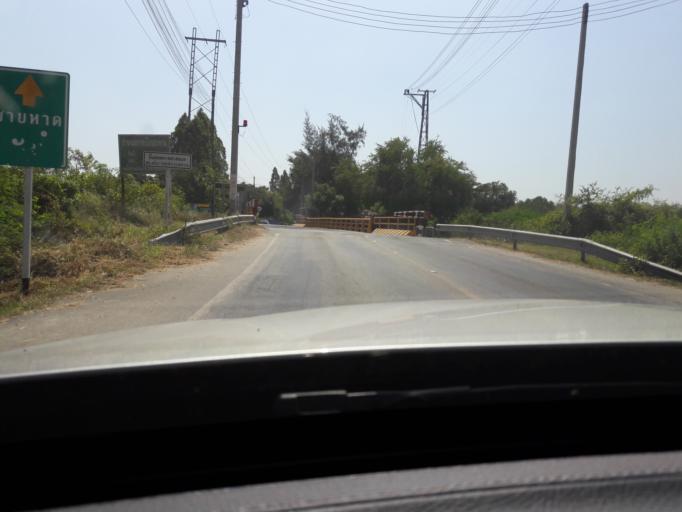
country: TH
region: Phetchaburi
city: Cha-am
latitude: 12.8213
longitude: 99.9833
